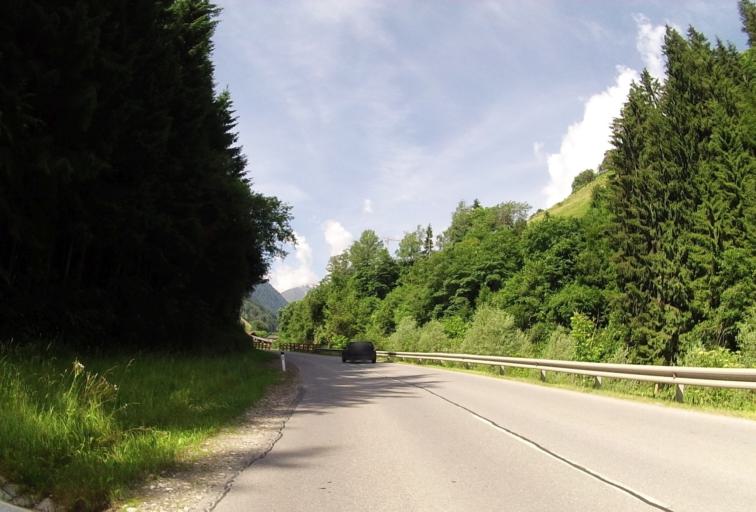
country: AT
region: Tyrol
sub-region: Politischer Bezirk Innsbruck Land
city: Sellrain
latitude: 47.2179
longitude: 11.2227
